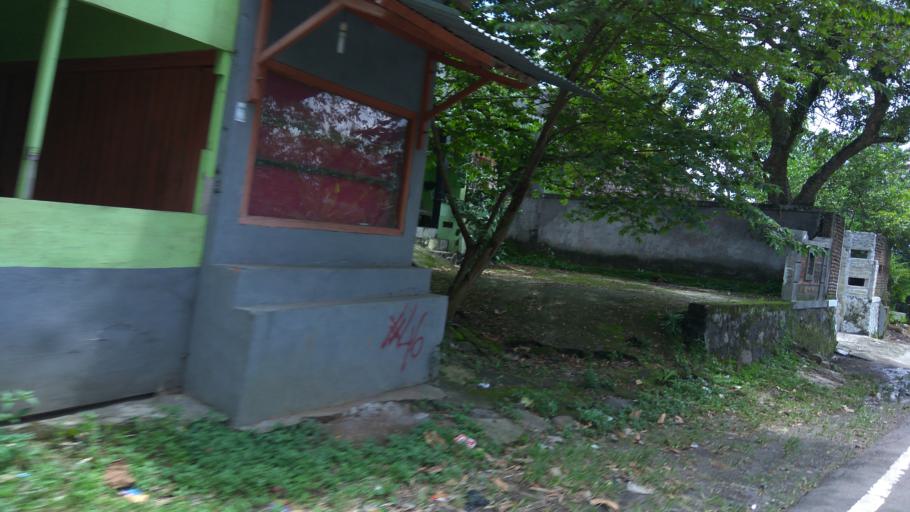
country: ID
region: Central Java
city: Ambarawa
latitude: -7.2432
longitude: 110.3929
